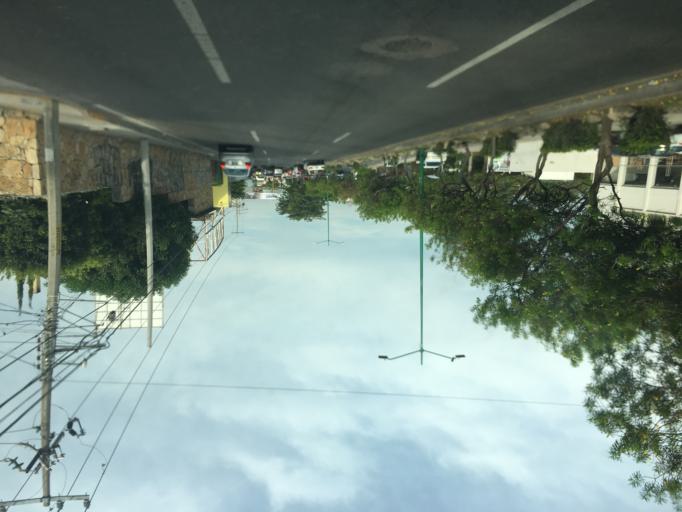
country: MX
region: Chiapas
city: Tuxtla Gutierrez
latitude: 16.7630
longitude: -93.1557
